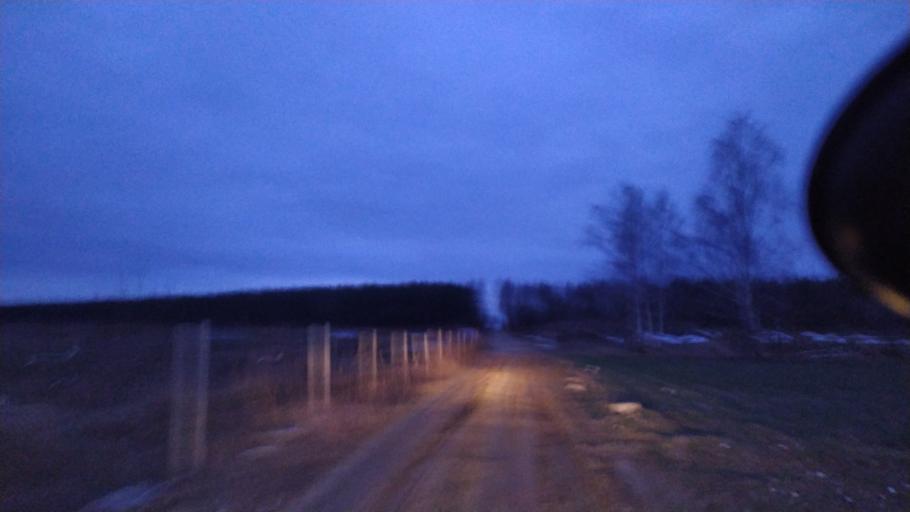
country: PL
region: Lublin Voivodeship
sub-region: Powiat lubelski
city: Jastkow
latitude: 51.3801
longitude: 22.4379
